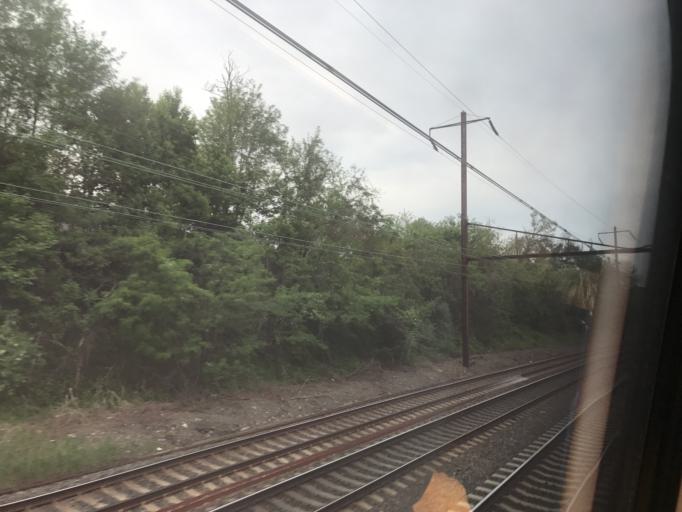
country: US
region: Maryland
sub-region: Baltimore County
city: Charlestown
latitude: 39.2827
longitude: -76.6707
